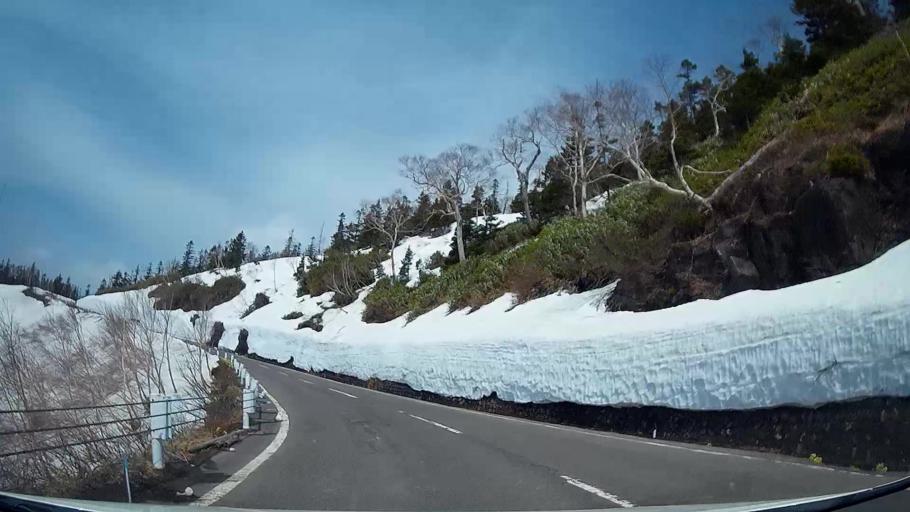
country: JP
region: Akita
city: Hanawa
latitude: 39.9514
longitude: 140.8935
